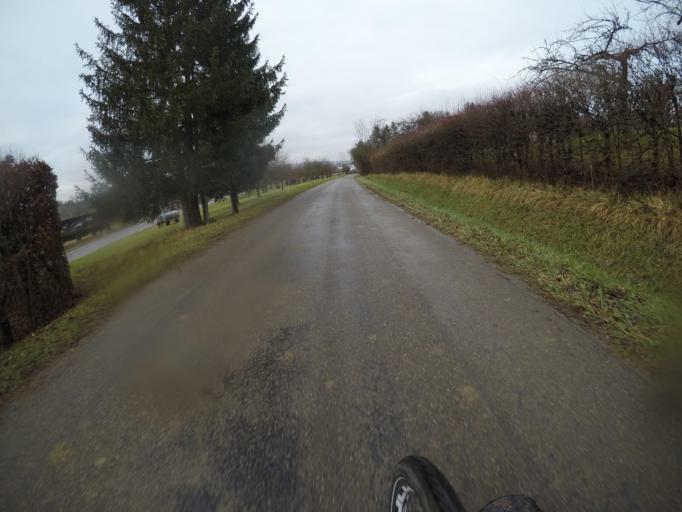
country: DE
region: Baden-Wuerttemberg
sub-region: Regierungsbezirk Stuttgart
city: Nurtingen
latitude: 48.6164
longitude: 9.3630
